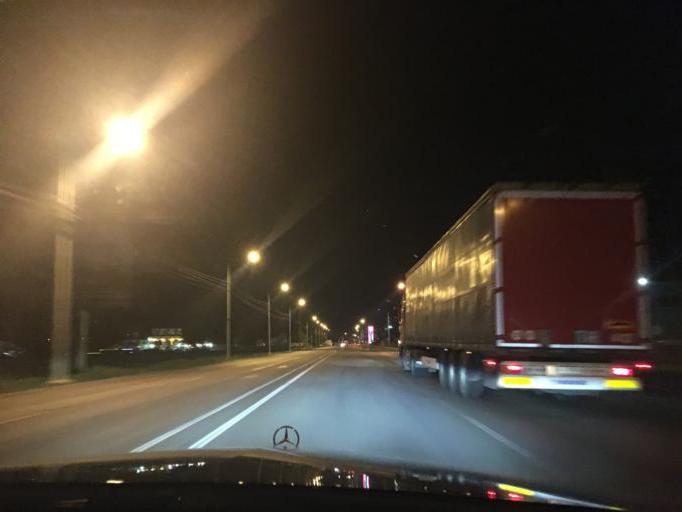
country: RO
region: Bihor
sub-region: Comuna Bors
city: Bors
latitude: 47.1094
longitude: 21.8194
